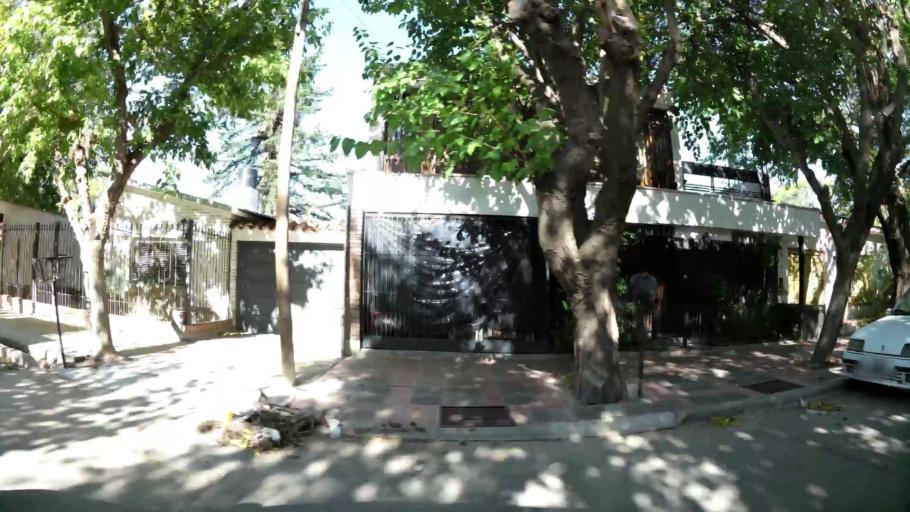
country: AR
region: Mendoza
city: Mendoza
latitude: -32.9111
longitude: -68.8243
